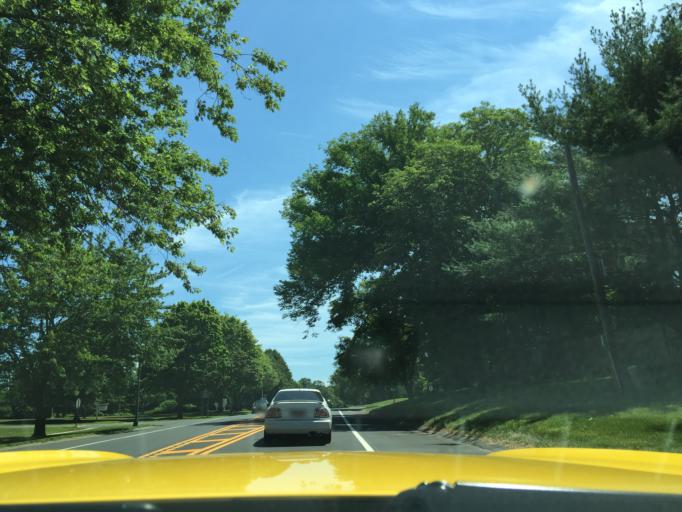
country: US
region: New York
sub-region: Suffolk County
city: East Hampton
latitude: 40.9676
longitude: -72.1729
